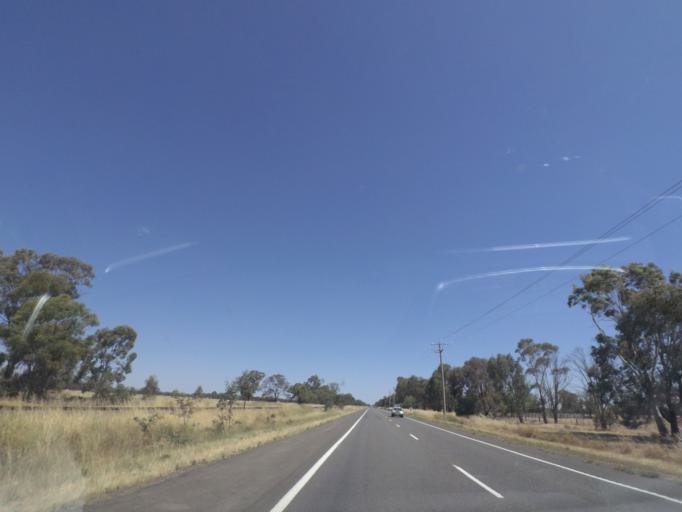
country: AU
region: Victoria
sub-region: Greater Shepparton
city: Shepparton
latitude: -36.2418
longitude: 145.4319
